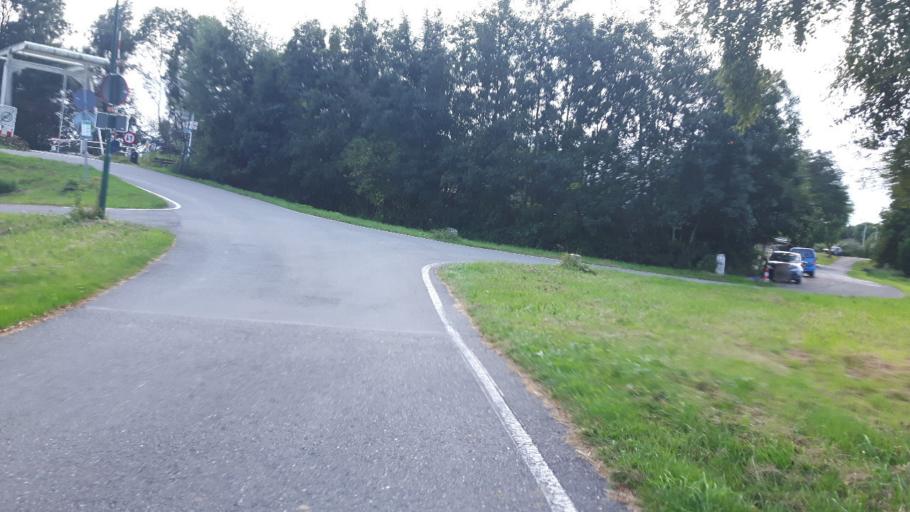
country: NL
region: Utrecht
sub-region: Gemeente De Ronde Venen
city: Mijdrecht
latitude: 52.1624
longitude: 4.8948
